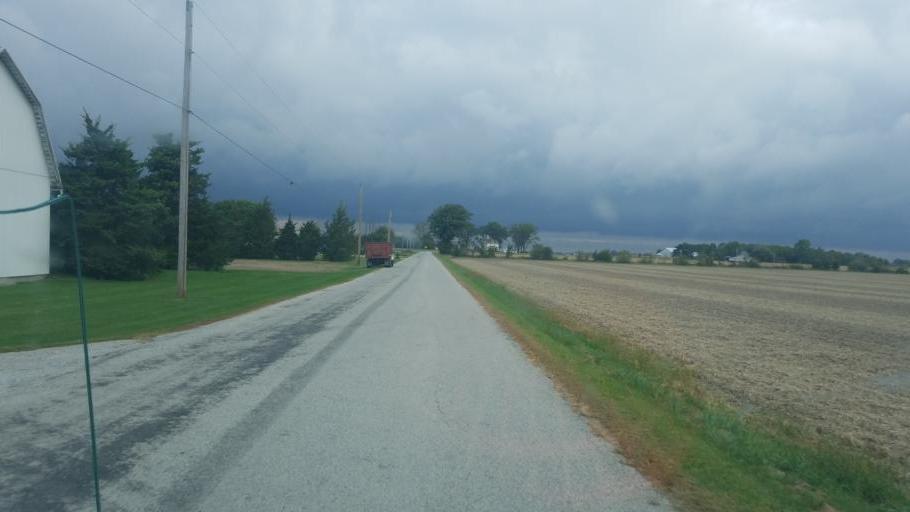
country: US
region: Ohio
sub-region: Wood County
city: North Baltimore
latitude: 41.1801
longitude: -83.6021
